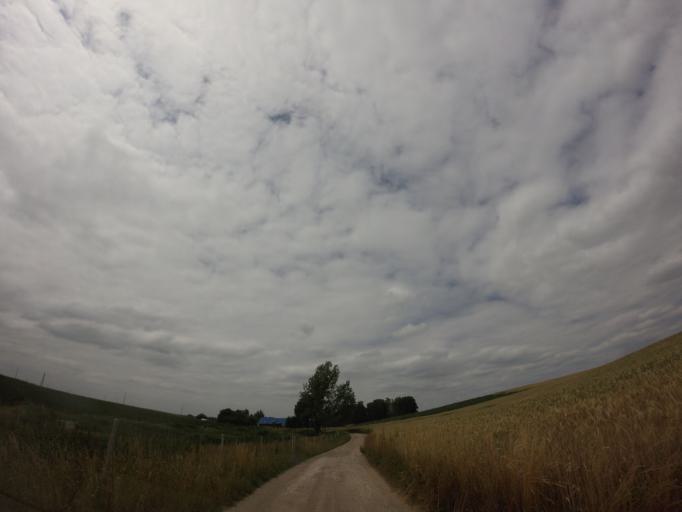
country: PL
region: West Pomeranian Voivodeship
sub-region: Powiat choszczenski
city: Krzecin
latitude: 53.0790
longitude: 15.5186
